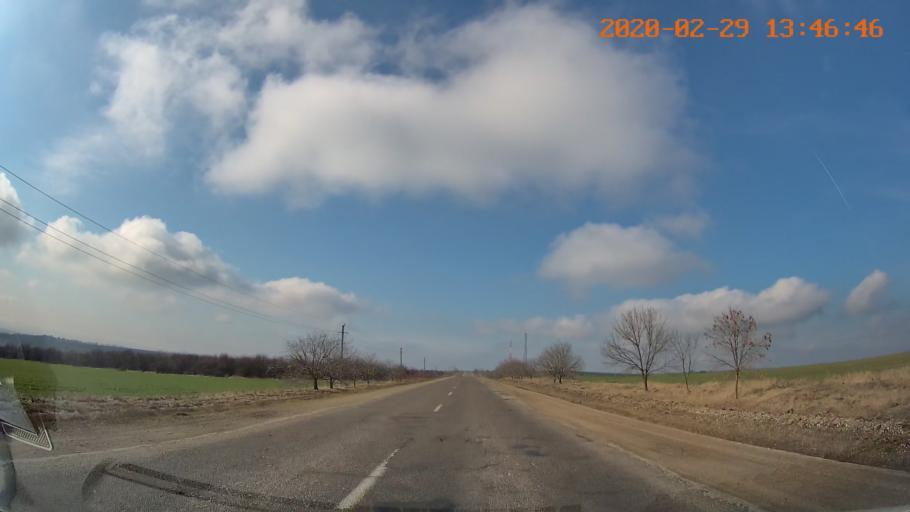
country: MD
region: Floresti
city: Leninskiy
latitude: 47.8594
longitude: 28.4998
